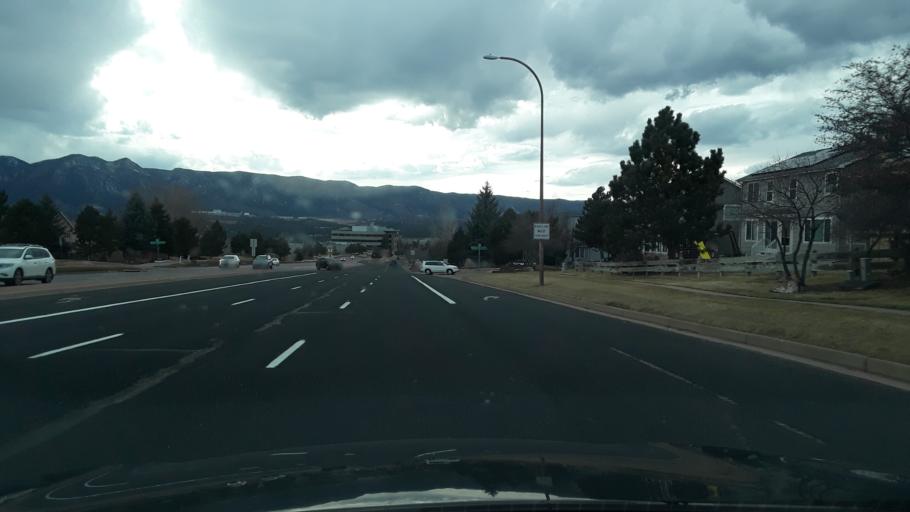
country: US
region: Colorado
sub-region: El Paso County
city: Gleneagle
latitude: 39.0078
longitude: -104.8002
